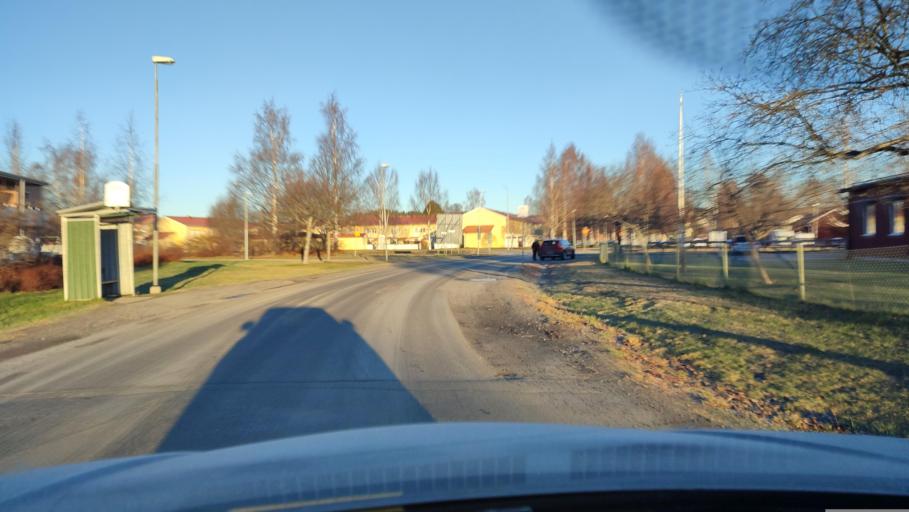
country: SE
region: Vaesterbotten
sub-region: Skelleftea Kommun
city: Skelleftea
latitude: 64.7441
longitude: 20.9827
